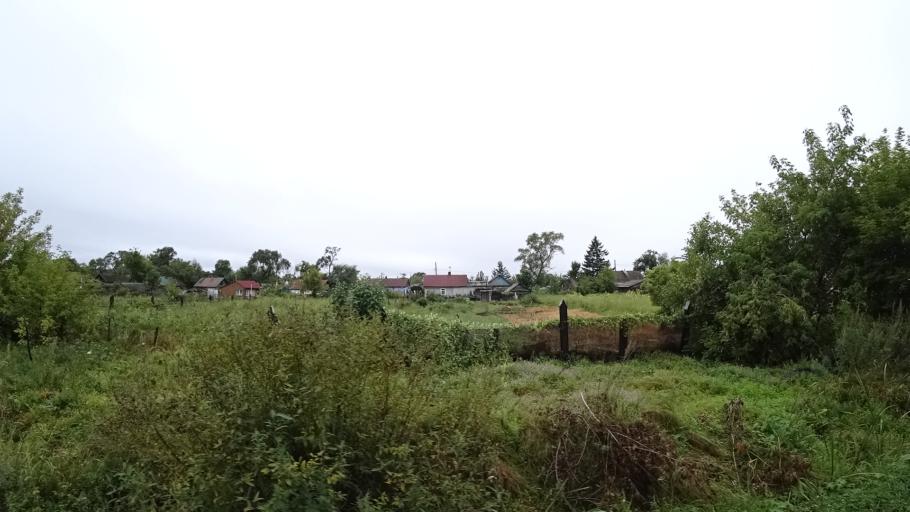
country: RU
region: Primorskiy
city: Monastyrishche
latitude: 44.2017
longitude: 132.4261
